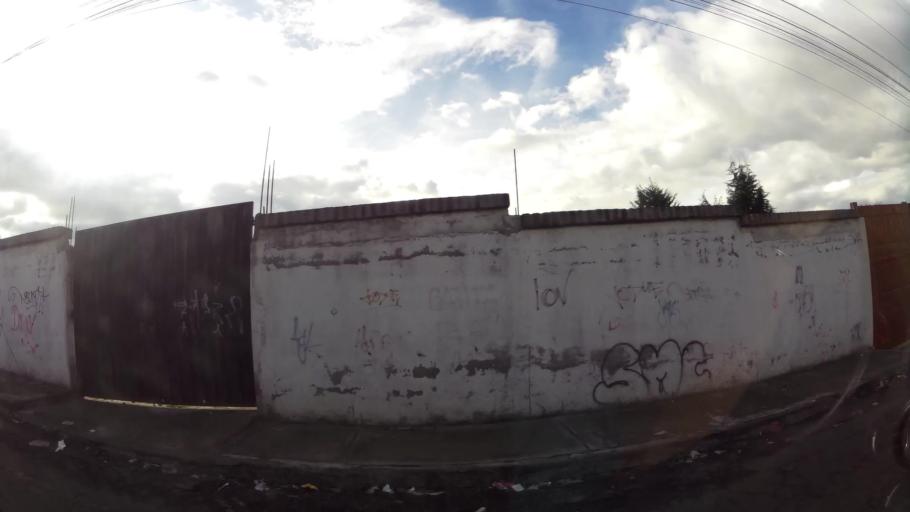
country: EC
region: Pichincha
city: Quito
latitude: -0.1341
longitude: -78.4578
